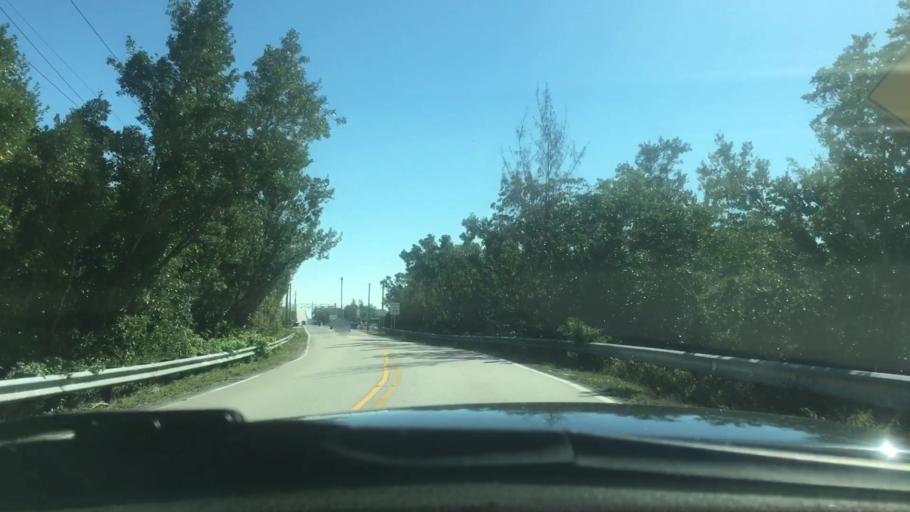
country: US
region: Florida
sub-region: Monroe County
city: North Key Largo
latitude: 25.2926
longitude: -80.3810
